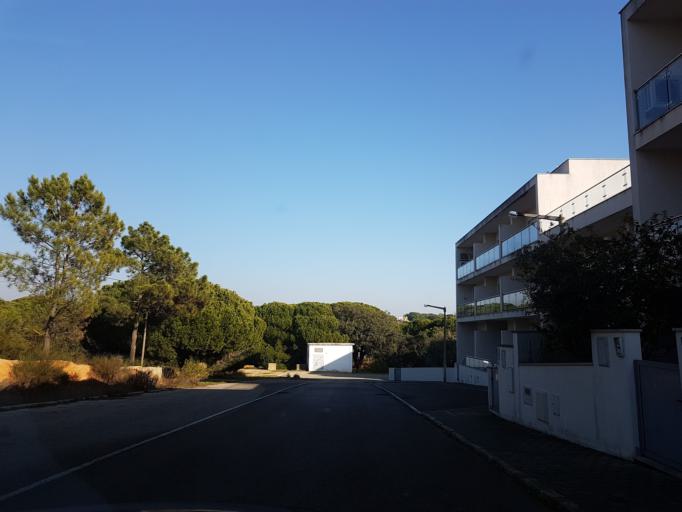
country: PT
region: Faro
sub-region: Albufeira
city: Ferreiras
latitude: 37.0962
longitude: -8.2026
